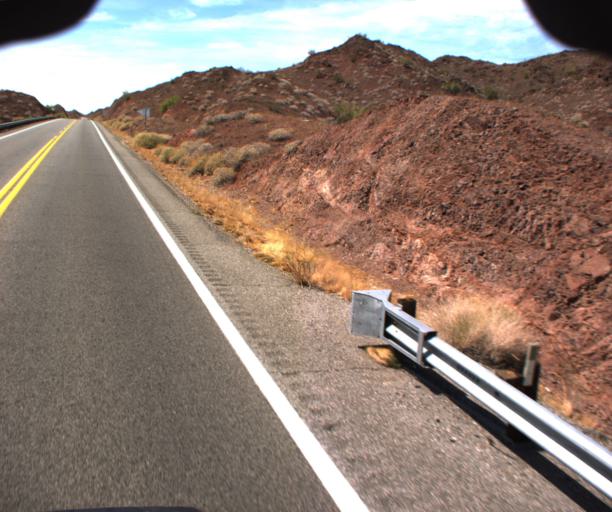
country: US
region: Arizona
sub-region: La Paz County
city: Cienega Springs
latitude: 34.3097
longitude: -114.1023
